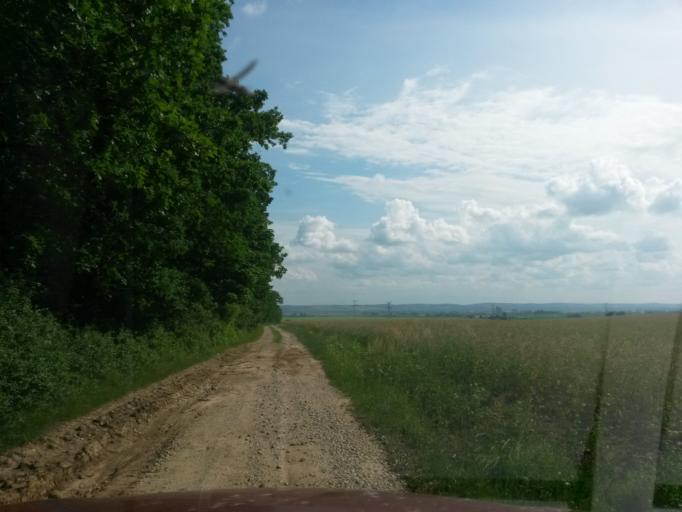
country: SK
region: Kosicky
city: Moldava nad Bodvou
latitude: 48.6166
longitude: 21.1043
